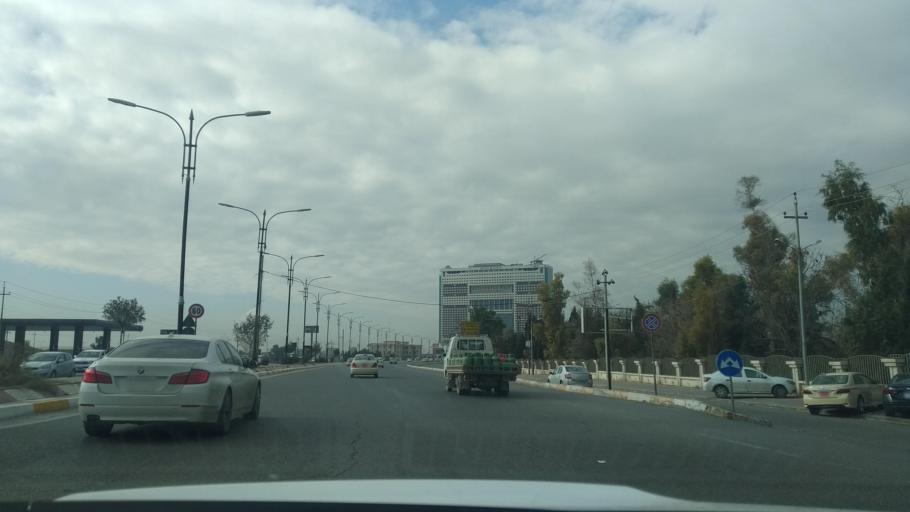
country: IQ
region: Arbil
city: Erbil
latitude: 36.1865
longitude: 43.9877
